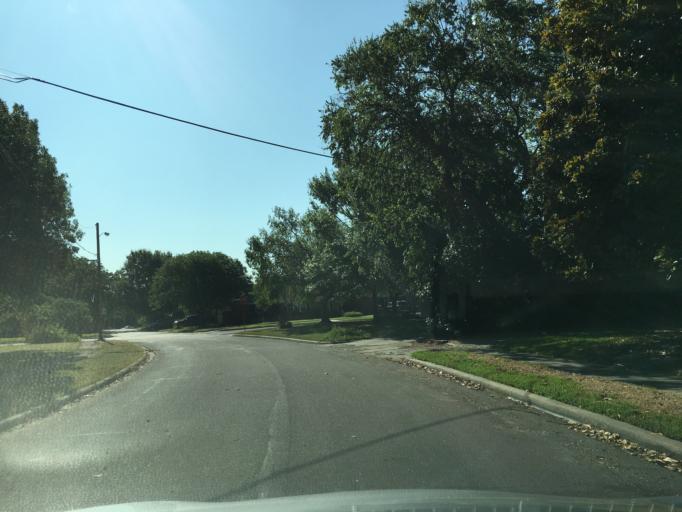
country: US
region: Texas
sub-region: Dallas County
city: Garland
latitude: 32.8615
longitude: -96.7074
